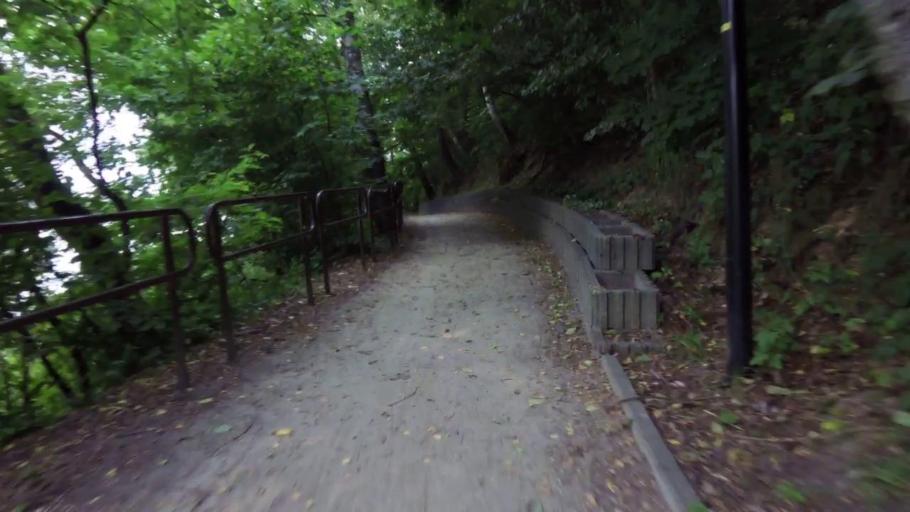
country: PL
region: West Pomeranian Voivodeship
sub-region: Powiat choszczenski
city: Choszczno
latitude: 53.1570
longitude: 15.4270
